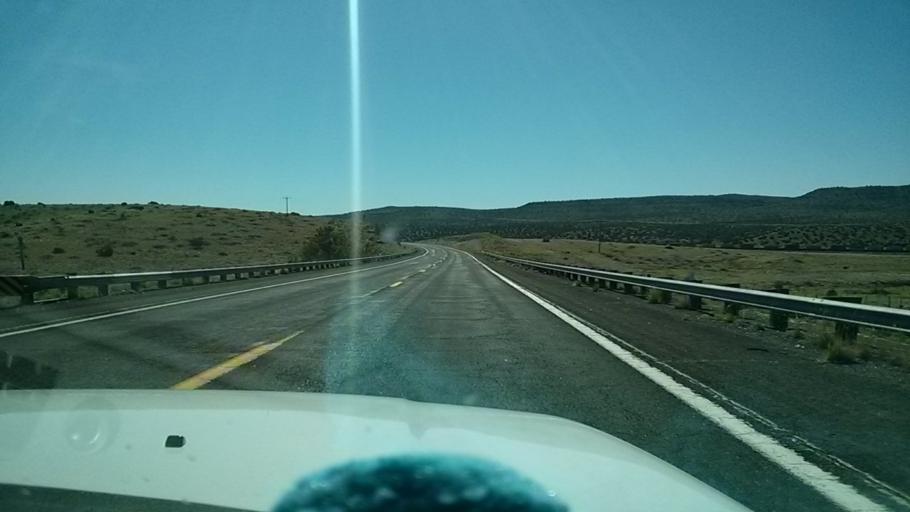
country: US
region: Arizona
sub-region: Mohave County
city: Peach Springs
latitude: 35.5221
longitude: -113.4599
